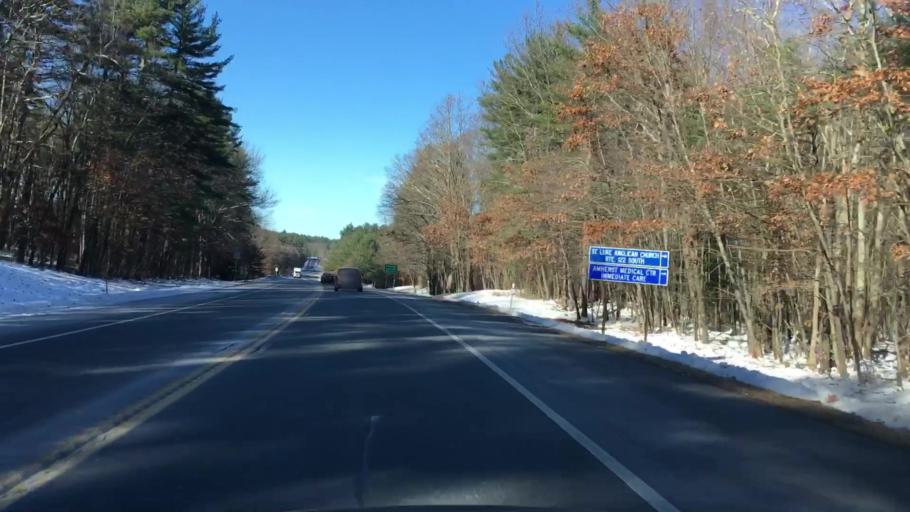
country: US
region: New Hampshire
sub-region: Hillsborough County
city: Milford
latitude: 42.8562
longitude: -71.6107
